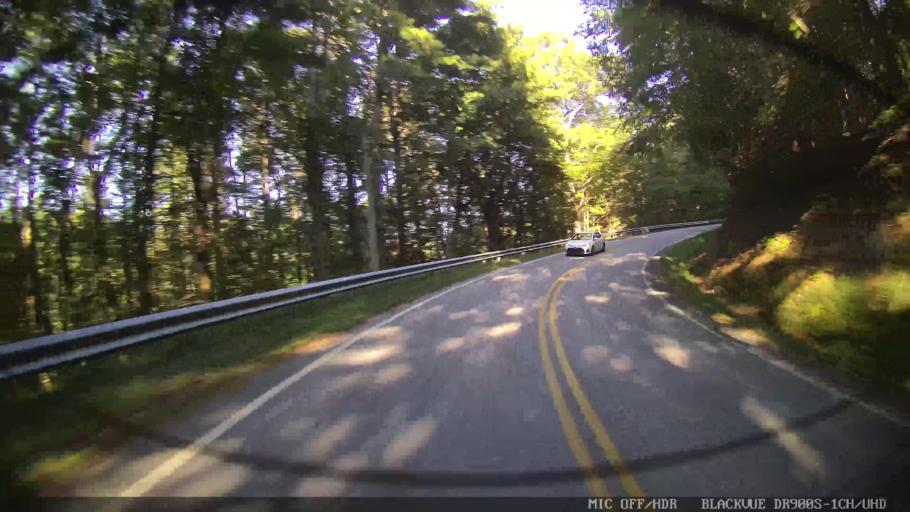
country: US
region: Georgia
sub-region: Lumpkin County
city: Dahlonega
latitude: 34.7051
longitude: -84.0428
